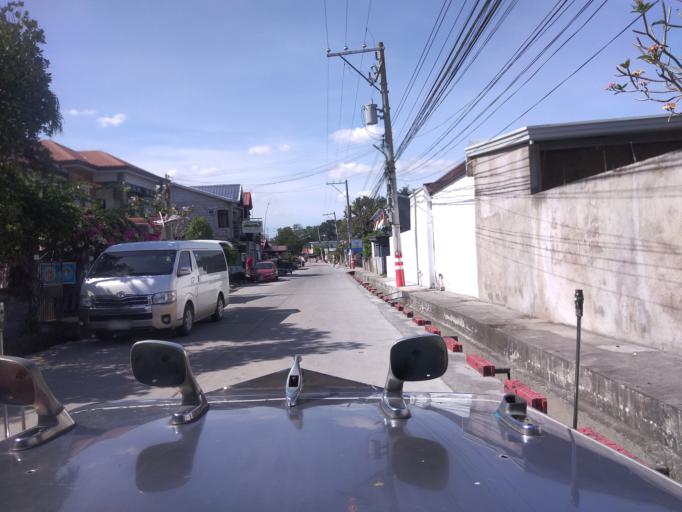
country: PH
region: Central Luzon
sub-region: Province of Pampanga
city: Magliman
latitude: 15.0337
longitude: 120.6662
